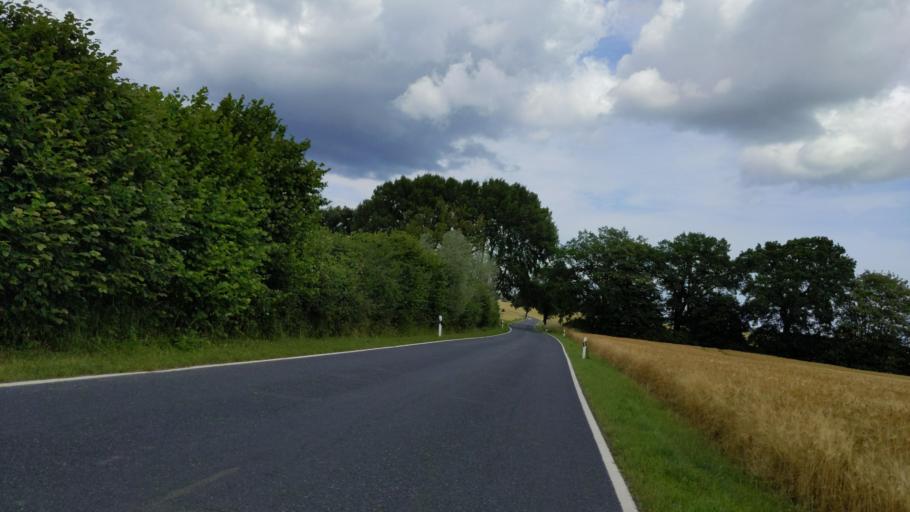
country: DE
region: Mecklenburg-Vorpommern
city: Dassow
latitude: 53.9427
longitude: 10.9717
